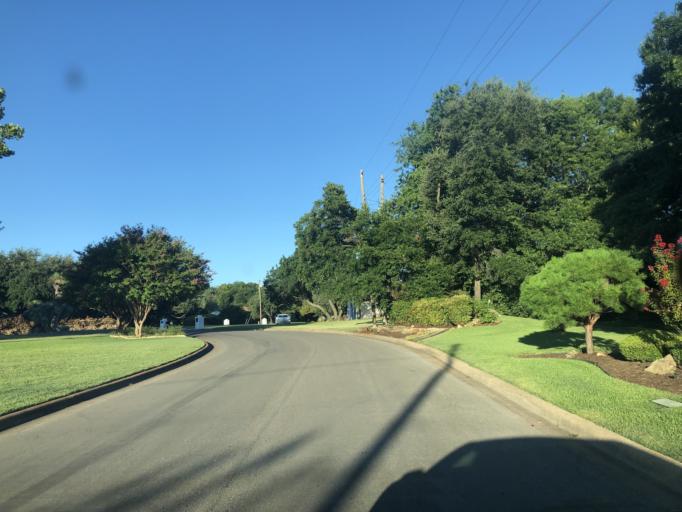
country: US
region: Texas
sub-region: Dallas County
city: Duncanville
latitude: 32.6384
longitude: -96.9402
